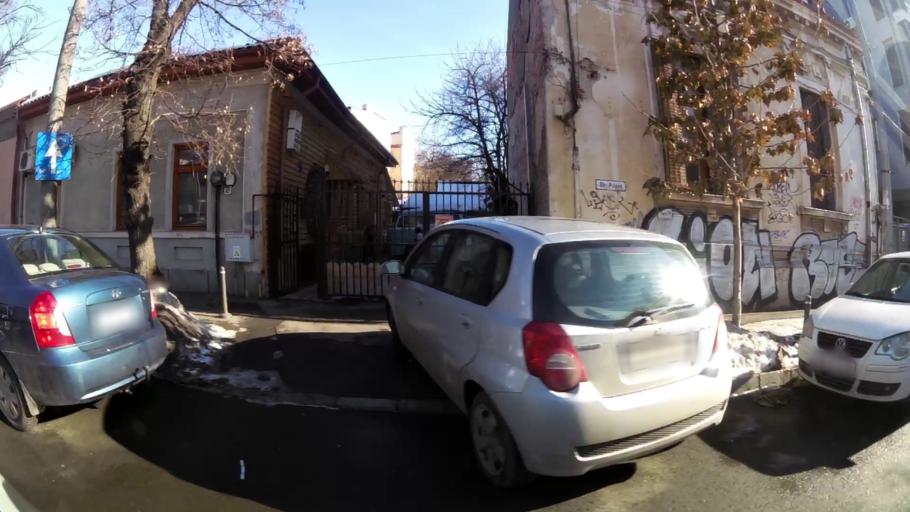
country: RO
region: Bucuresti
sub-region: Municipiul Bucuresti
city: Bucharest
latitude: 44.4488
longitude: 26.1030
